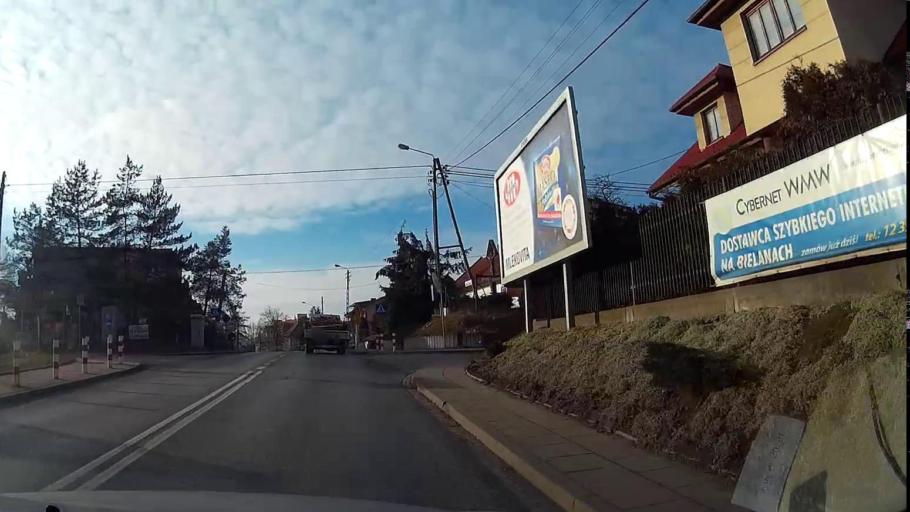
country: PL
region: Lesser Poland Voivodeship
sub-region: Powiat krakowski
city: Kryspinow
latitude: 50.0442
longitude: 19.8274
